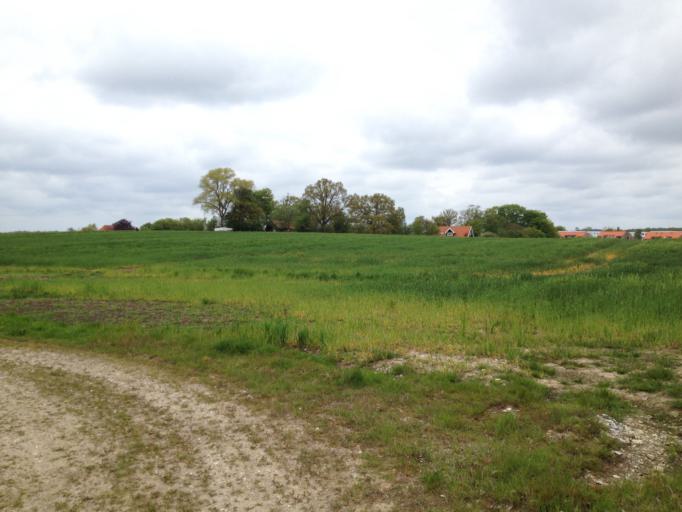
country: DK
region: Capital Region
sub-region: Fredensborg Kommune
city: Humlebaek
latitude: 55.9500
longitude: 12.5207
